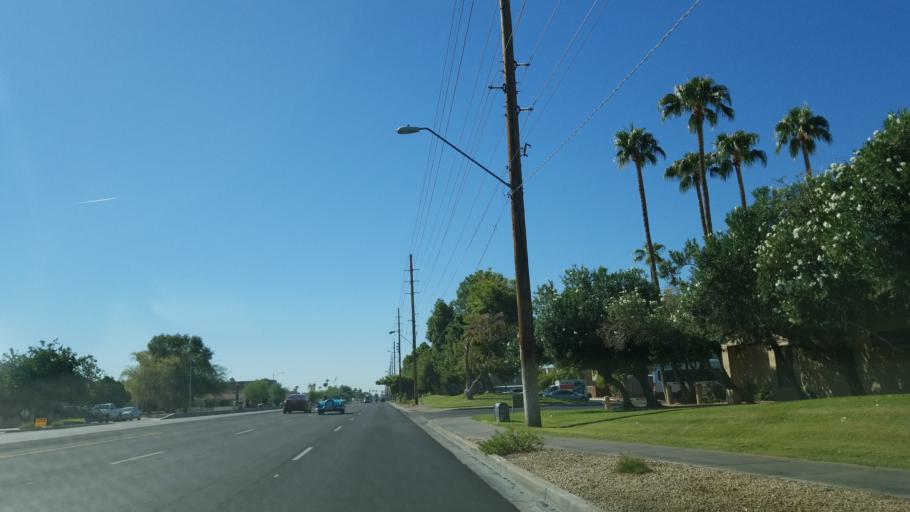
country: US
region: Arizona
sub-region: Maricopa County
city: Scottsdale
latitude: 33.4936
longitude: -111.9090
